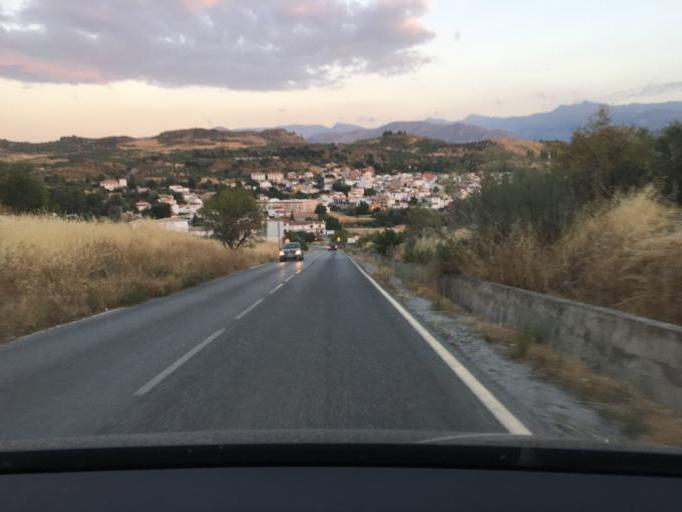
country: ES
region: Andalusia
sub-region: Provincia de Granada
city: Beas de Granada
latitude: 37.2233
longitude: -3.4865
